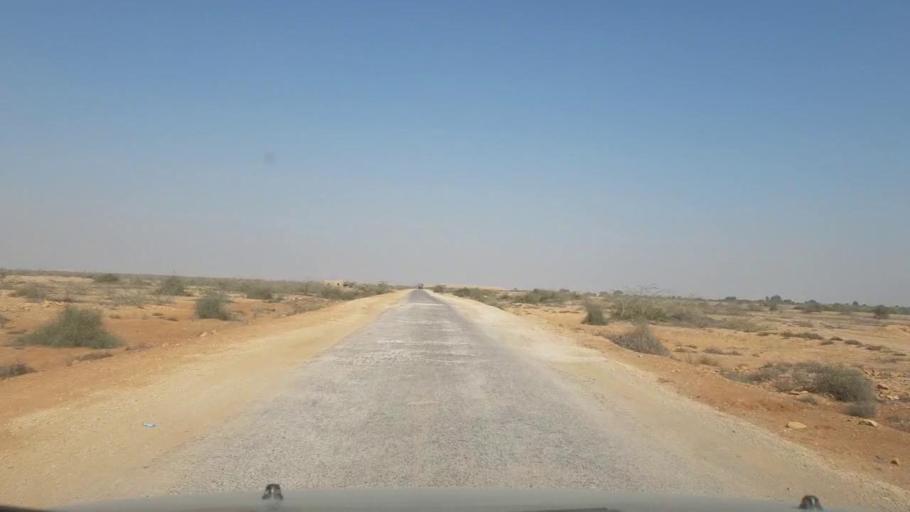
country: PK
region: Sindh
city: Thatta
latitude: 24.9479
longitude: 67.9526
